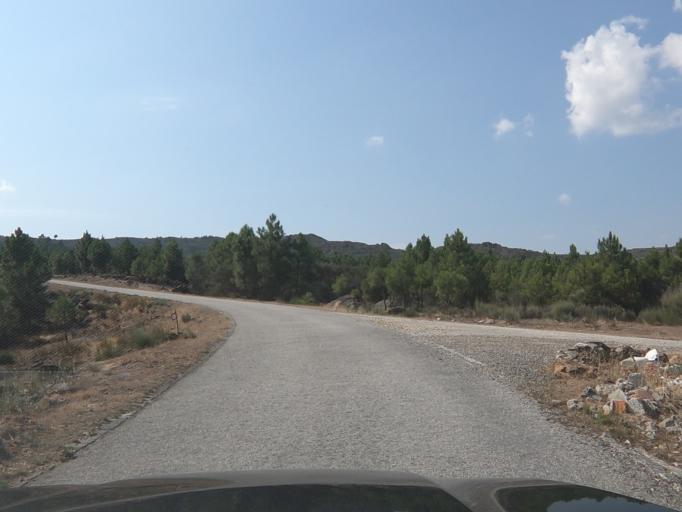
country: PT
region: Vila Real
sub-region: Sabrosa
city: Sabrosa
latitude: 41.3064
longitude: -7.5855
